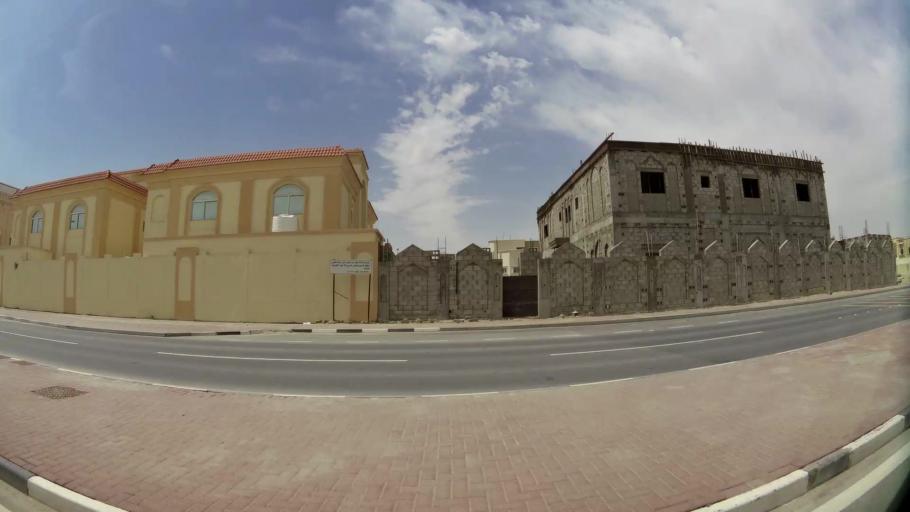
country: QA
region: Baladiyat ar Rayyan
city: Ar Rayyan
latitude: 25.2954
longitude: 51.4121
